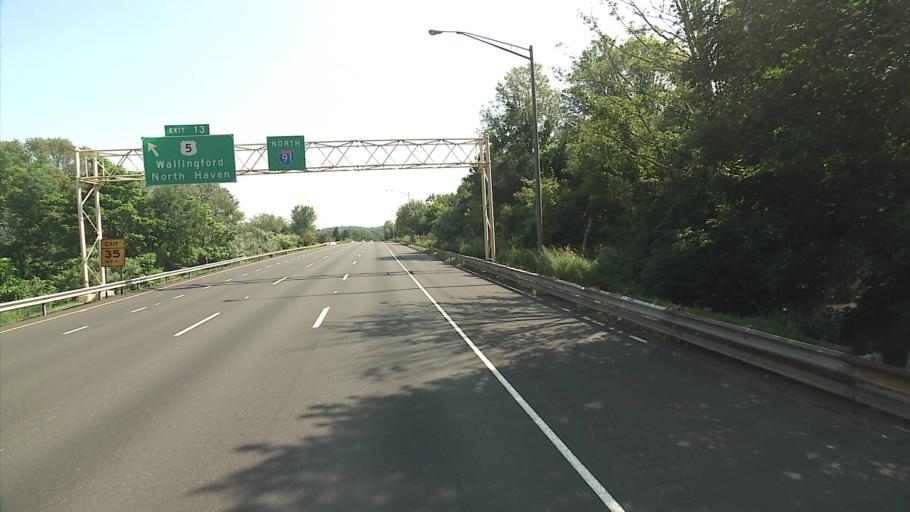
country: US
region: Connecticut
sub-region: New Haven County
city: Wallingford Center
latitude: 41.4201
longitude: -72.8264
